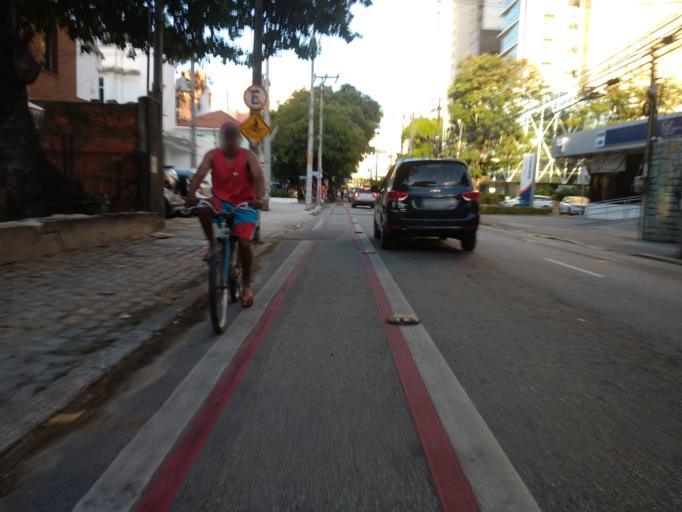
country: BR
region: Ceara
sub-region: Fortaleza
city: Fortaleza
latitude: -3.7321
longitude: -38.5110
